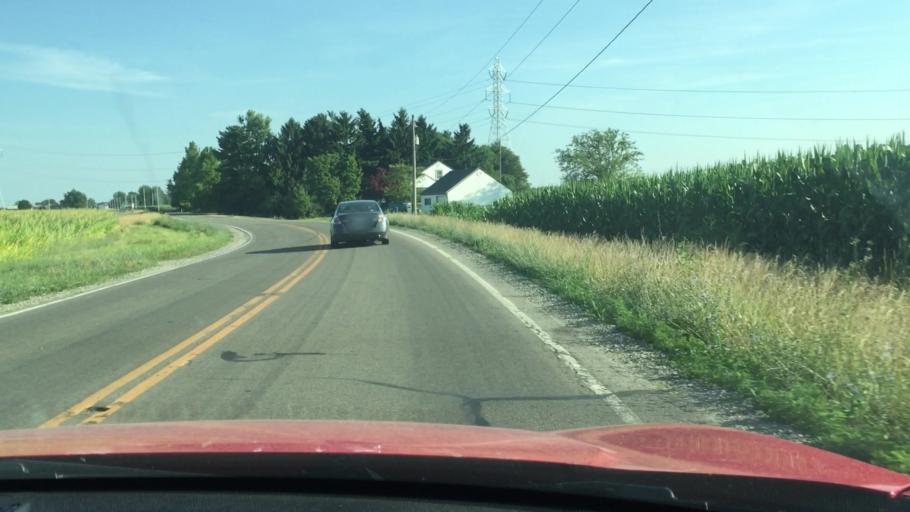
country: US
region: Ohio
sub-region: Hardin County
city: Ada
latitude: 40.6796
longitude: -83.8580
